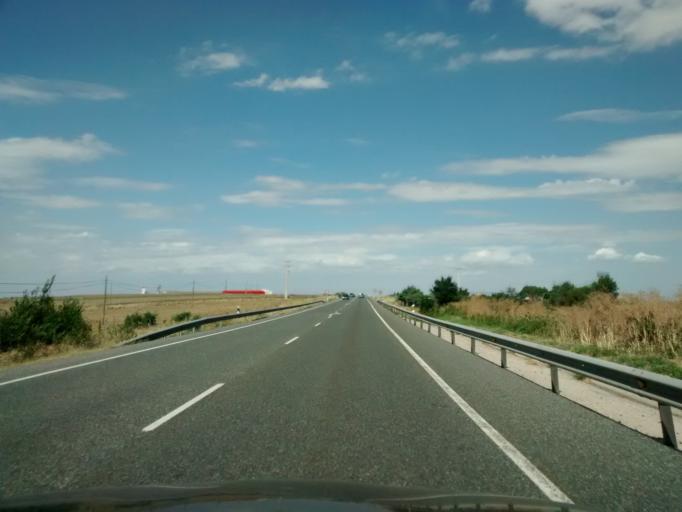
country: ES
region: Castille and Leon
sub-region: Provincia de Segovia
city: Torrecaballeros
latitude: 40.9854
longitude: -4.0436
